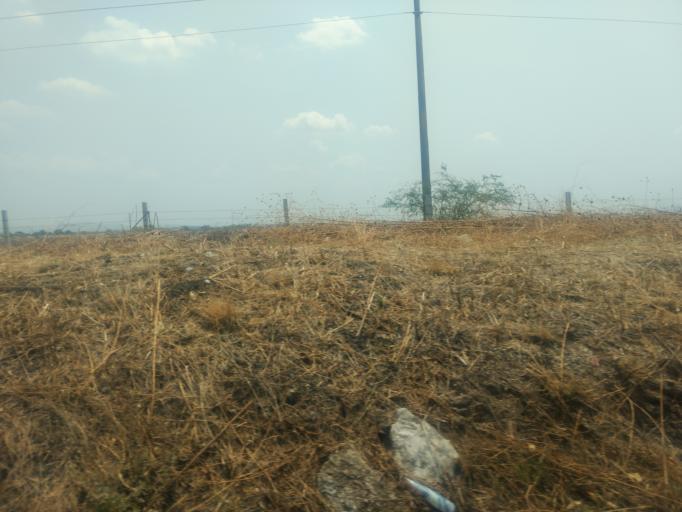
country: MX
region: Morelos
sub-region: Amacuzac
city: Amacuzac
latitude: 18.6271
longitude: -99.3741
